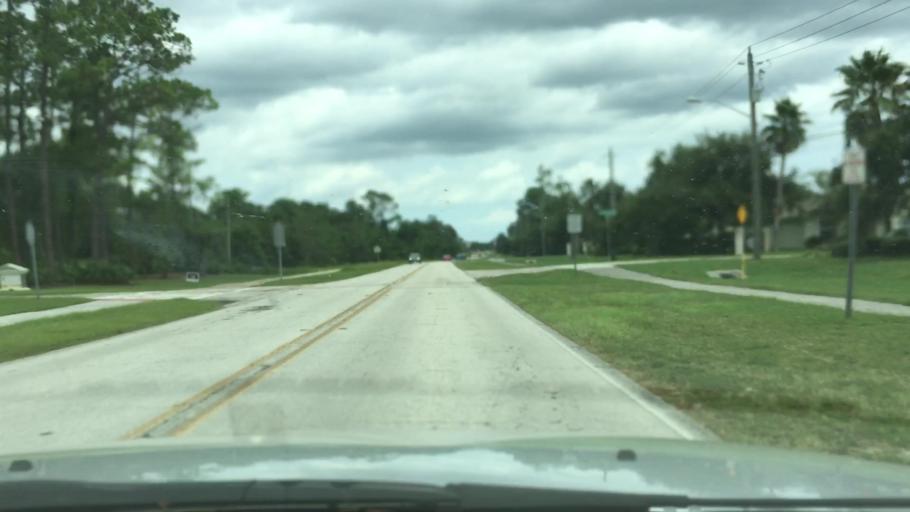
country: US
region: Florida
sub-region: Volusia County
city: Holly Hill
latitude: 29.2252
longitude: -81.0704
